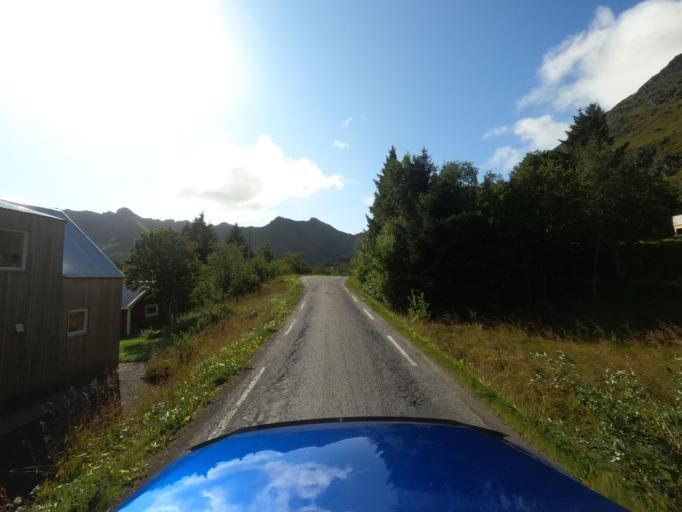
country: NO
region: Nordland
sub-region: Vestvagoy
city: Leknes
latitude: 68.1183
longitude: 13.7161
